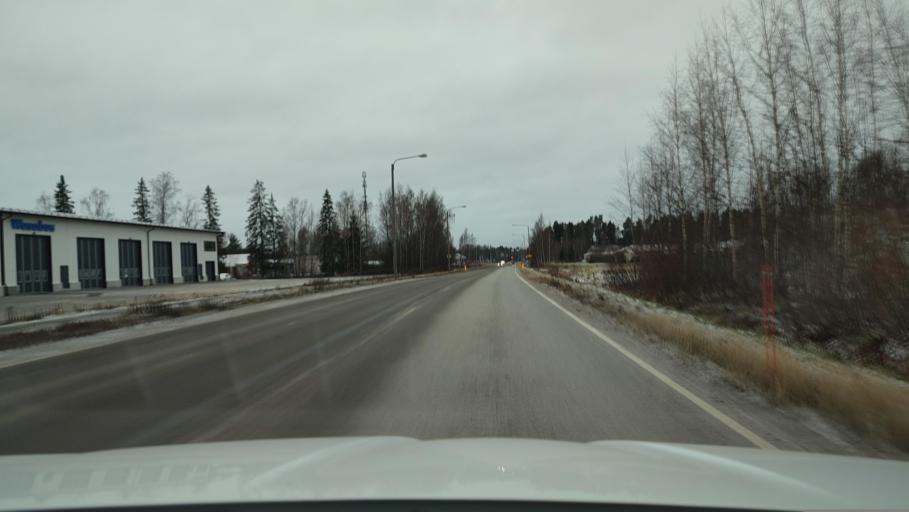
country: FI
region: Ostrobothnia
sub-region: Vaasa
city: Smedsby
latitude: 63.1173
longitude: 21.7137
